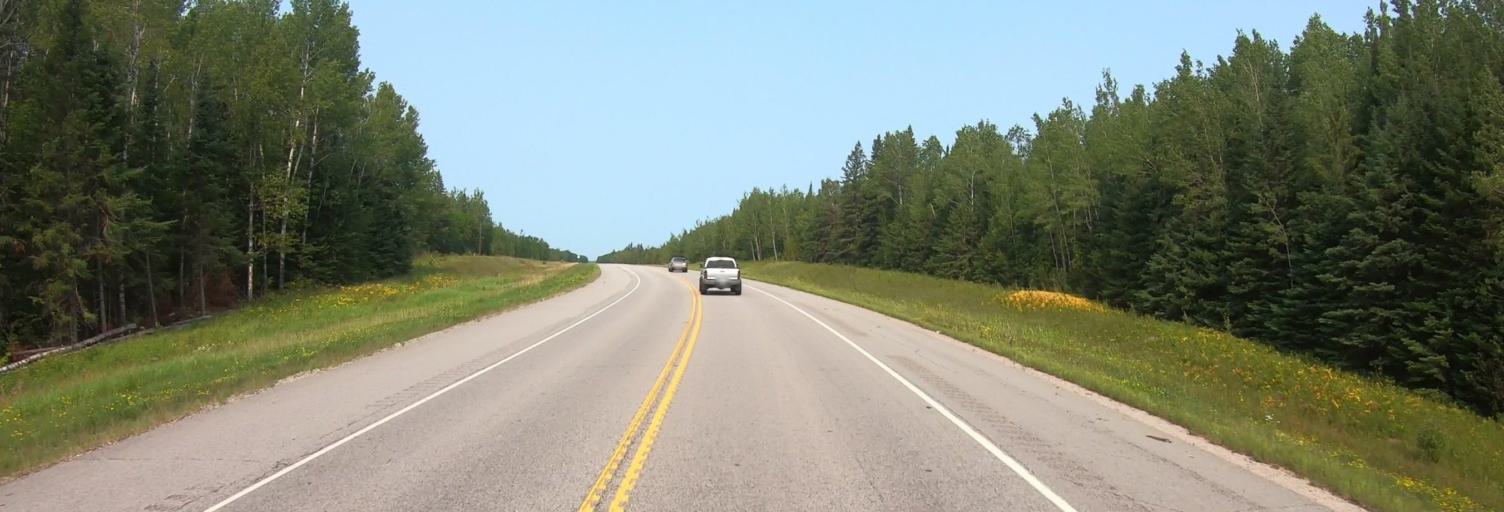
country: CA
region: Ontario
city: Fort Frances
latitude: 48.3660
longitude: -92.9651
